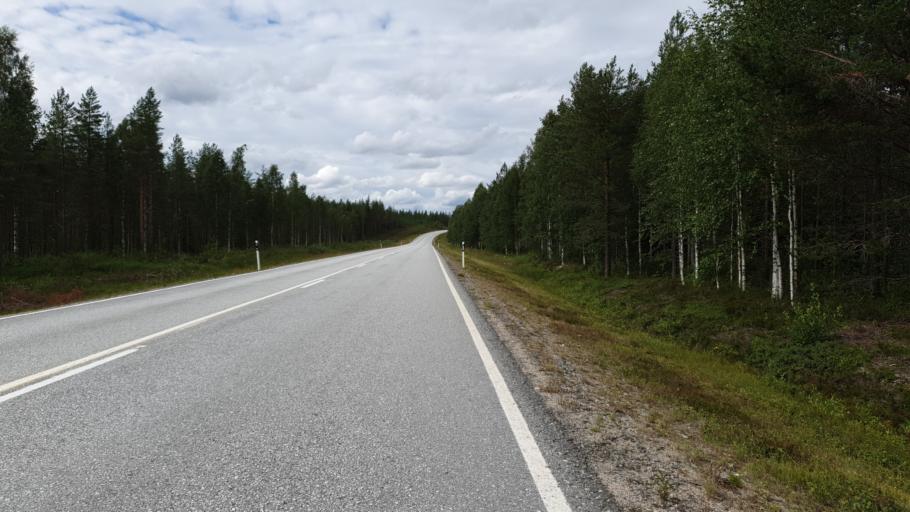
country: FI
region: Kainuu
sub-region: Kehys-Kainuu
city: Kuhmo
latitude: 64.4814
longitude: 29.7736
